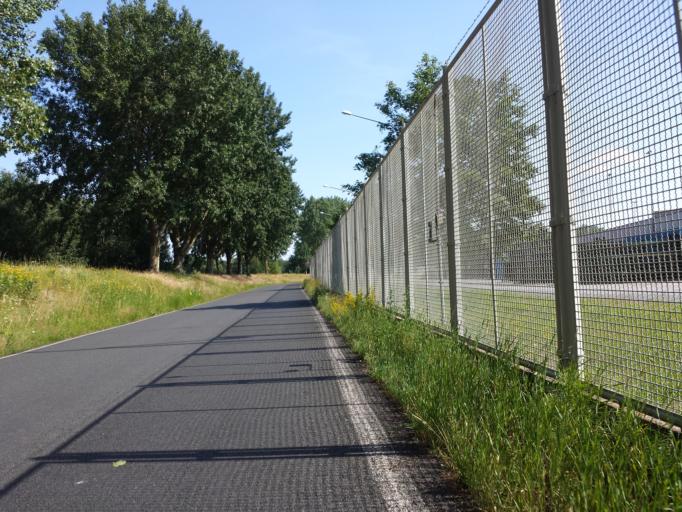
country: DE
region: Bremen
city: Bremen
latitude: 53.1015
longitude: 8.7478
